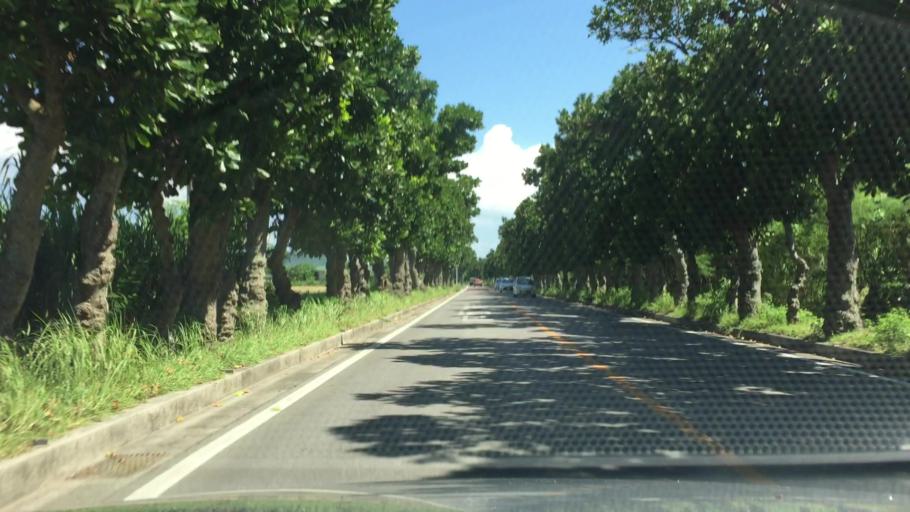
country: JP
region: Okinawa
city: Ishigaki
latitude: 24.3668
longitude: 124.2465
